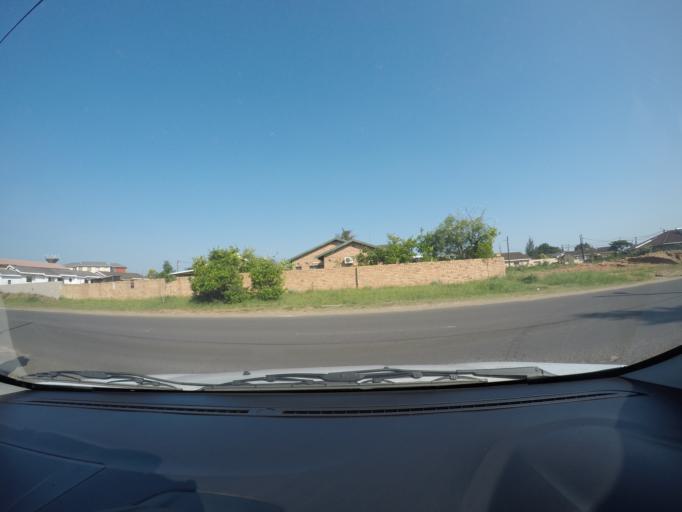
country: ZA
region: KwaZulu-Natal
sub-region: uThungulu District Municipality
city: Richards Bay
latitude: -28.7240
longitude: 32.0379
